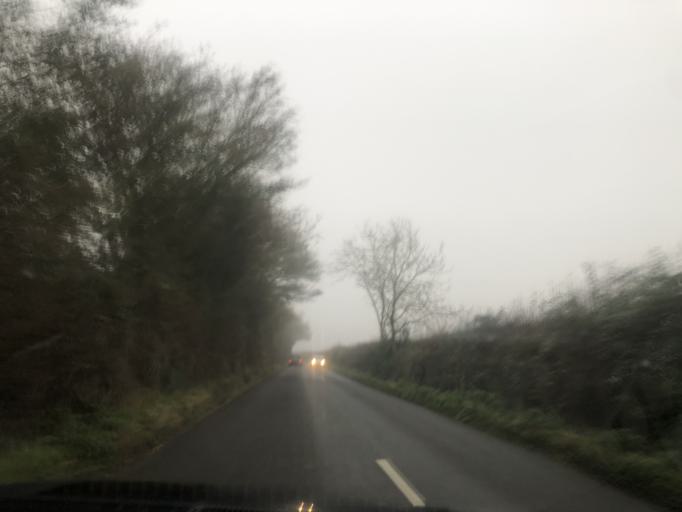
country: GB
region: England
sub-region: Oxfordshire
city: Bicester
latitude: 51.9213
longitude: -1.1836
